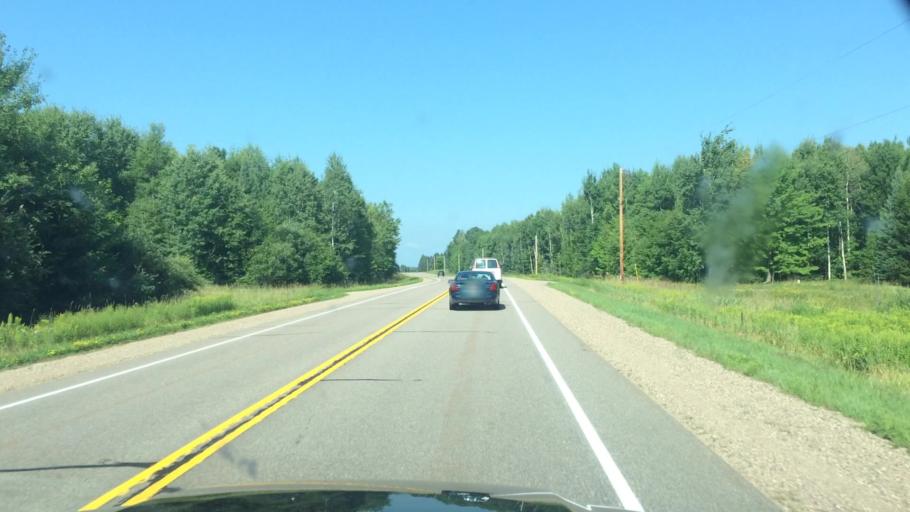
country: US
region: Wisconsin
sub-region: Langlade County
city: Antigo
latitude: 45.1482
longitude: -89.4161
